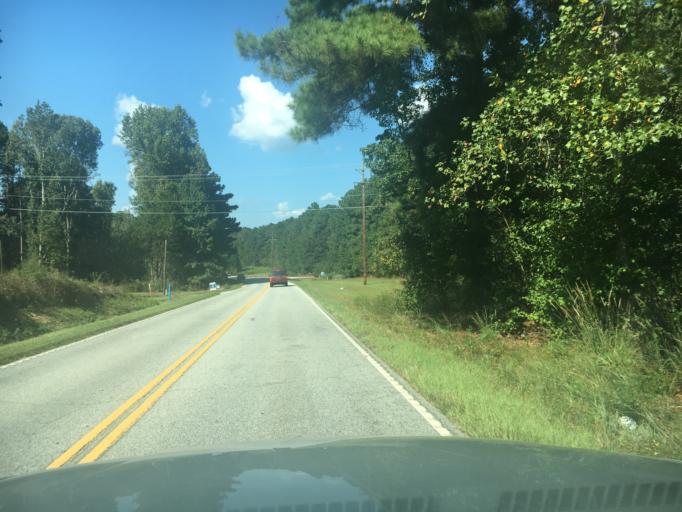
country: US
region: South Carolina
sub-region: Greenwood County
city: Greenwood
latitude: 34.2522
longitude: -82.1794
